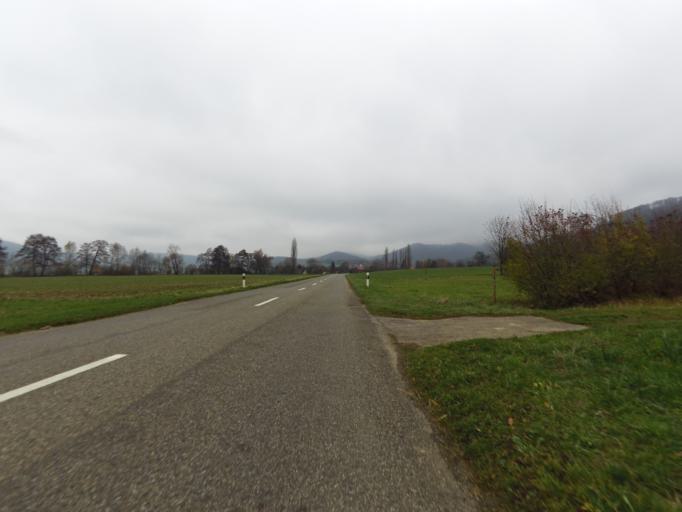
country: CH
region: Jura
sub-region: Porrentruy District
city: Alle
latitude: 47.4123
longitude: 7.1848
